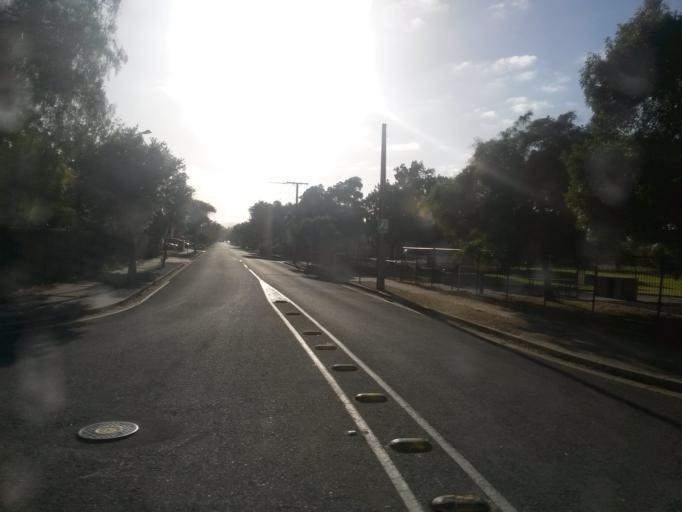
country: AU
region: South Australia
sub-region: Prospect
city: Prospect
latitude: -34.8853
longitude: 138.5761
